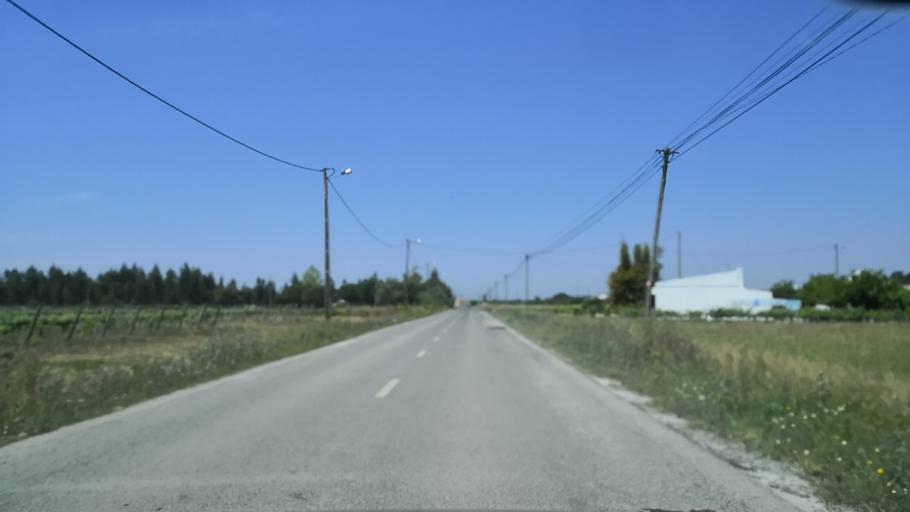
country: PT
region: Setubal
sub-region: Palmela
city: Pinhal Novo
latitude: 38.6436
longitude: -8.7435
